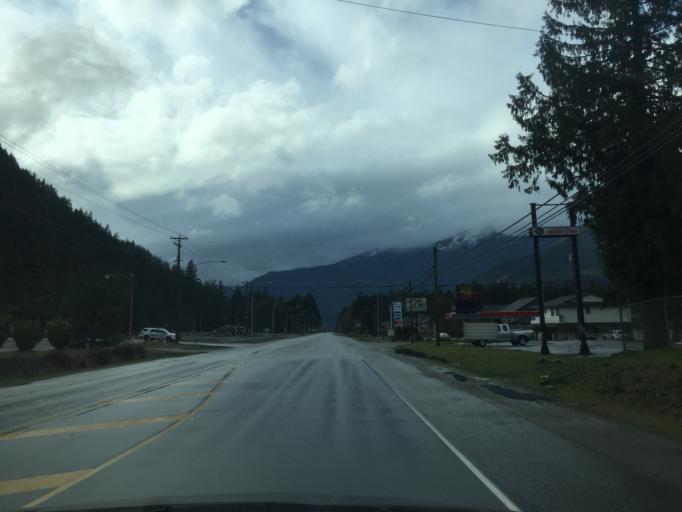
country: CA
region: British Columbia
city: Hope
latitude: 49.3605
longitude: -121.4649
